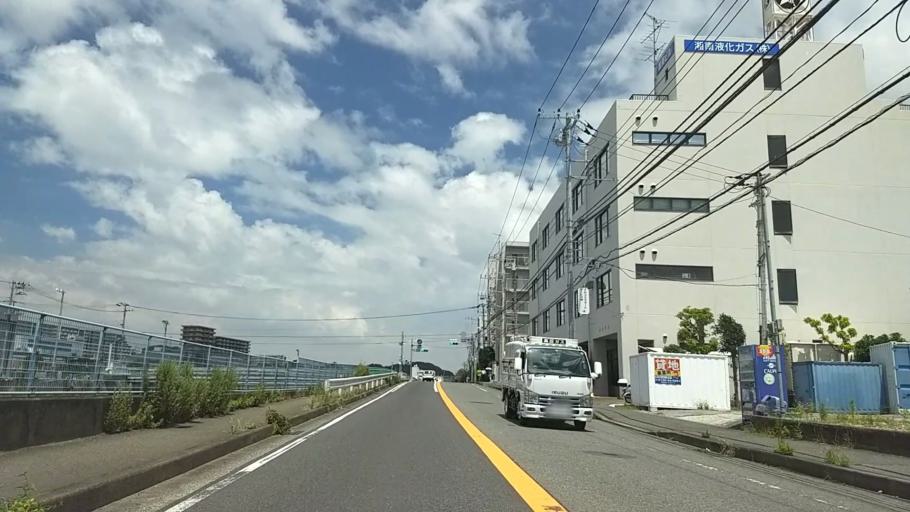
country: JP
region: Kanagawa
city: Fujisawa
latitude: 35.3386
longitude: 139.5144
